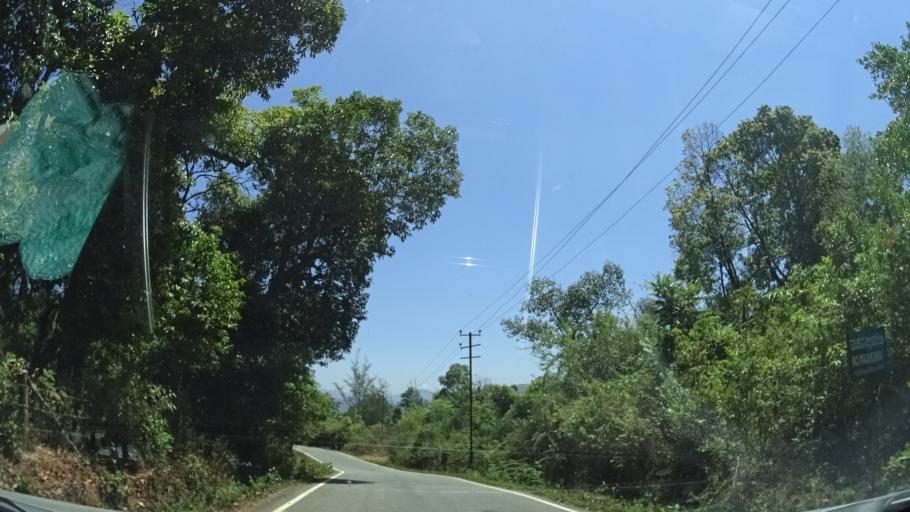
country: IN
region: Karnataka
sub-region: Chikmagalur
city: Sringeri
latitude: 13.1898
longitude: 75.3000
